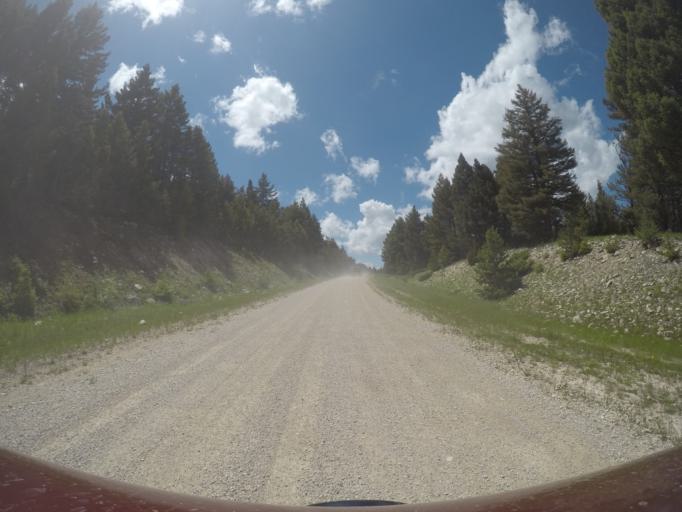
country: US
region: Wyoming
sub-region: Big Horn County
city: Lovell
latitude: 45.2041
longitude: -108.5276
